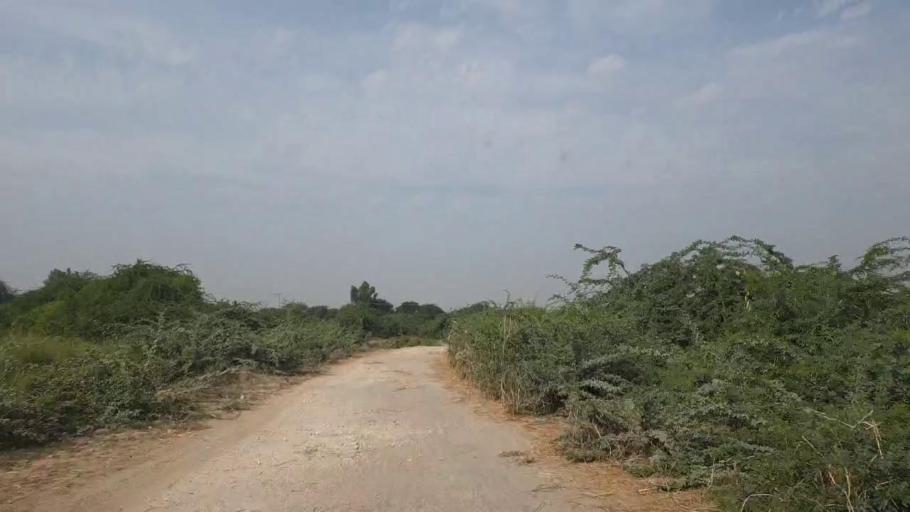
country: PK
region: Sindh
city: Tando Bago
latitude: 24.9253
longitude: 68.9888
